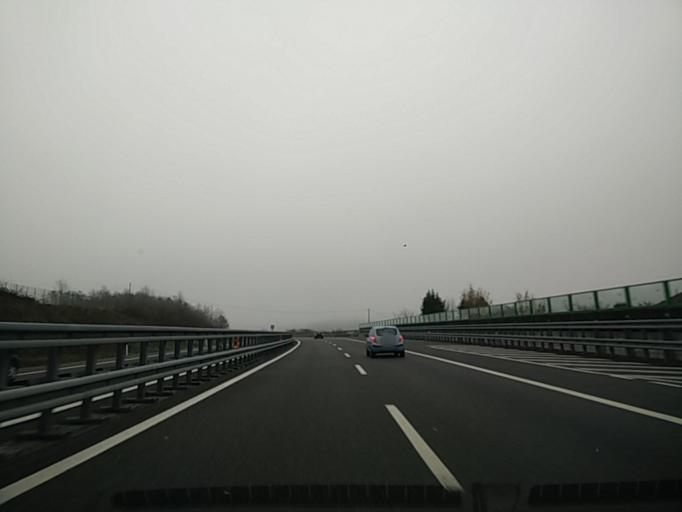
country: IT
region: Piedmont
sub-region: Provincia di Asti
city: Tigliole
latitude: 44.9039
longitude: 8.0582
